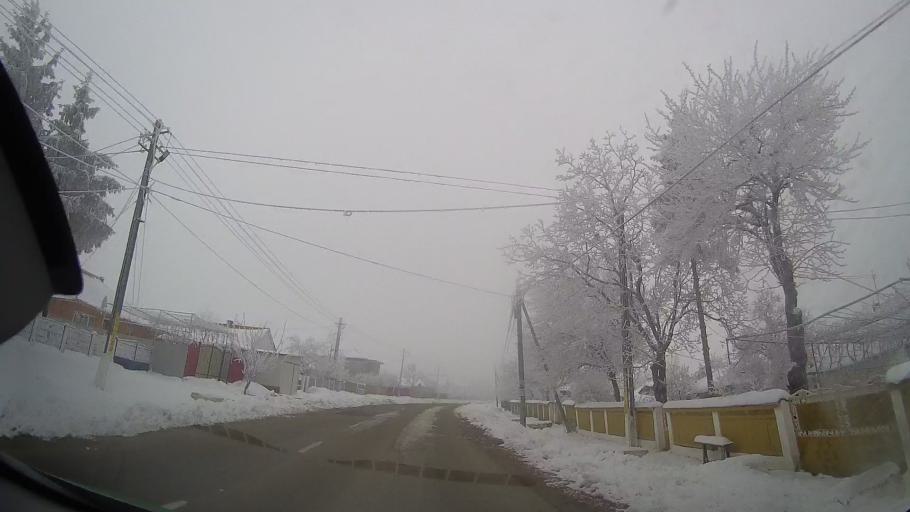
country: RO
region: Neamt
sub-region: Comuna Valea Ursului
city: Valea Ursului
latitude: 46.7977
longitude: 27.0784
